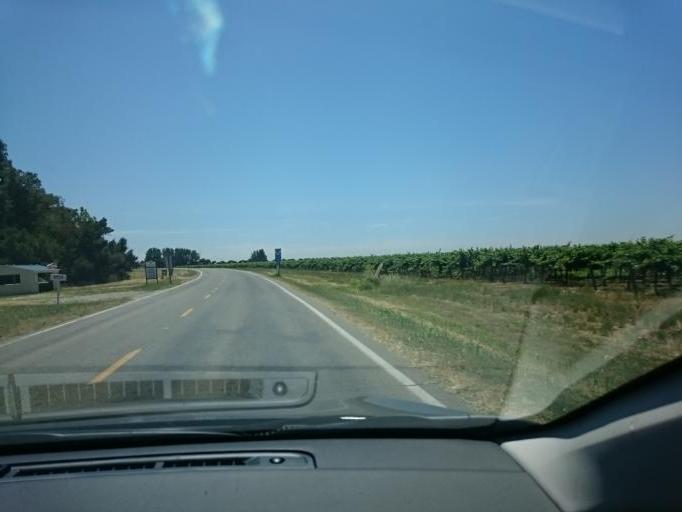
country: US
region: California
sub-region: Sacramento County
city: Walnut Grove
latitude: 38.2281
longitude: -121.5131
